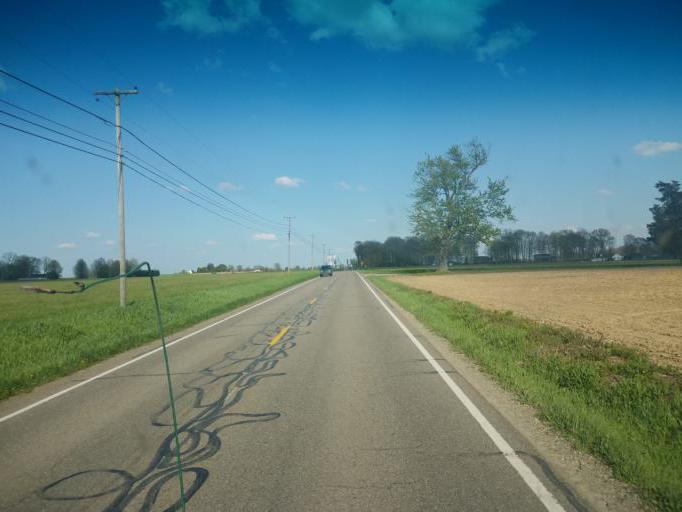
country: US
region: Ohio
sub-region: Wayne County
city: Smithville
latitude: 40.8289
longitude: -81.8667
